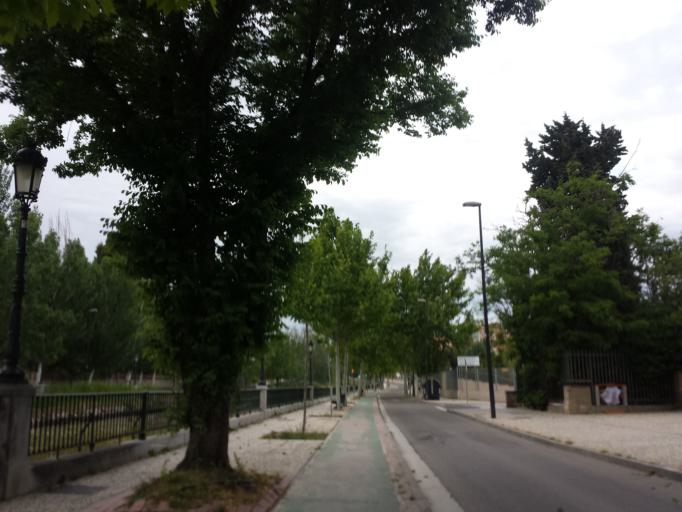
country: ES
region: Aragon
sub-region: Provincia de Zaragoza
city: Delicias
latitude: 41.6257
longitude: -0.9070
